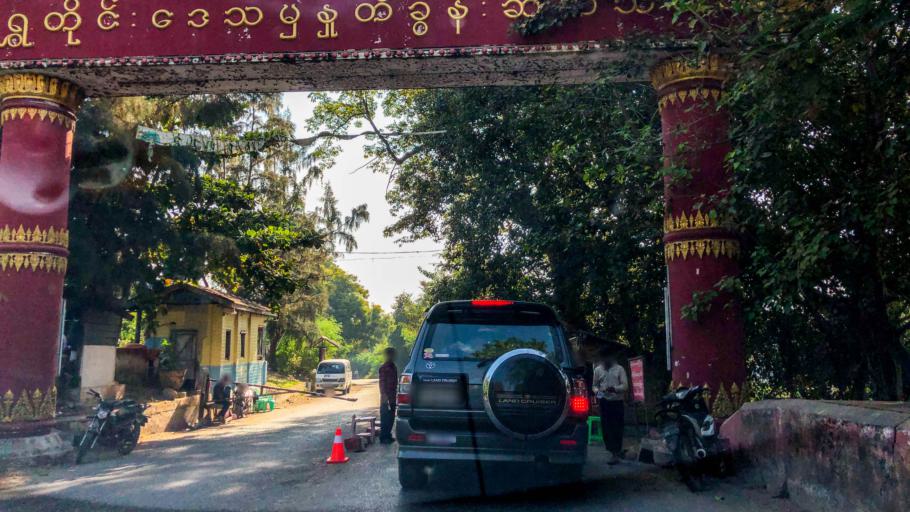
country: MM
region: Sagain
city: Sagaing
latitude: 21.8678
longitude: 95.9964
